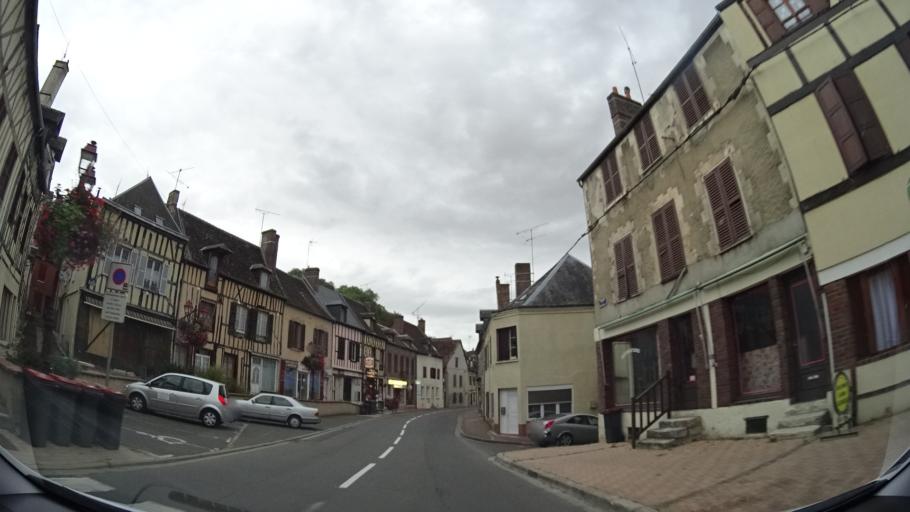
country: FR
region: Centre
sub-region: Departement du Loiret
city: Trigueres
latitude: 47.9327
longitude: 2.9276
